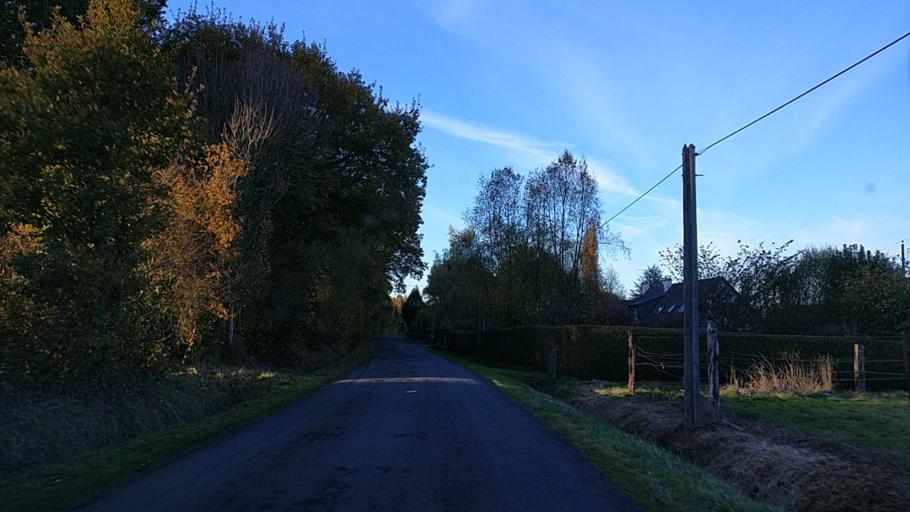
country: FR
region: Brittany
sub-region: Departement d'Ille-et-Vilaine
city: Saint-Sulpice-la-Foret
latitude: 48.2051
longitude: -1.5776
